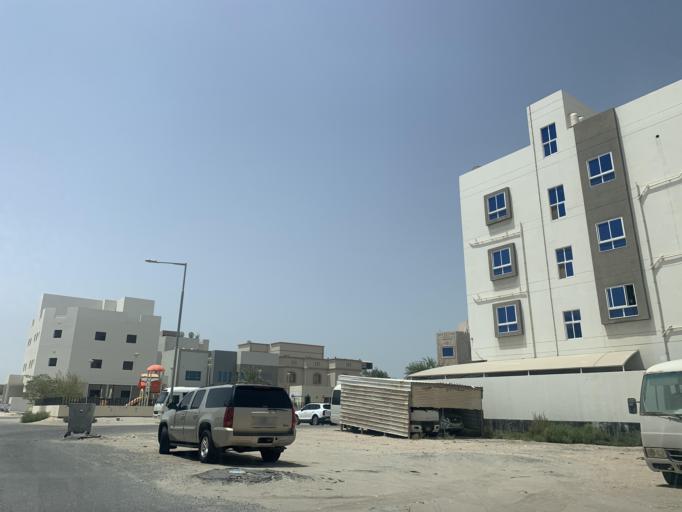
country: BH
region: Central Governorate
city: Madinat Hamad
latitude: 26.1436
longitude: 50.5060
